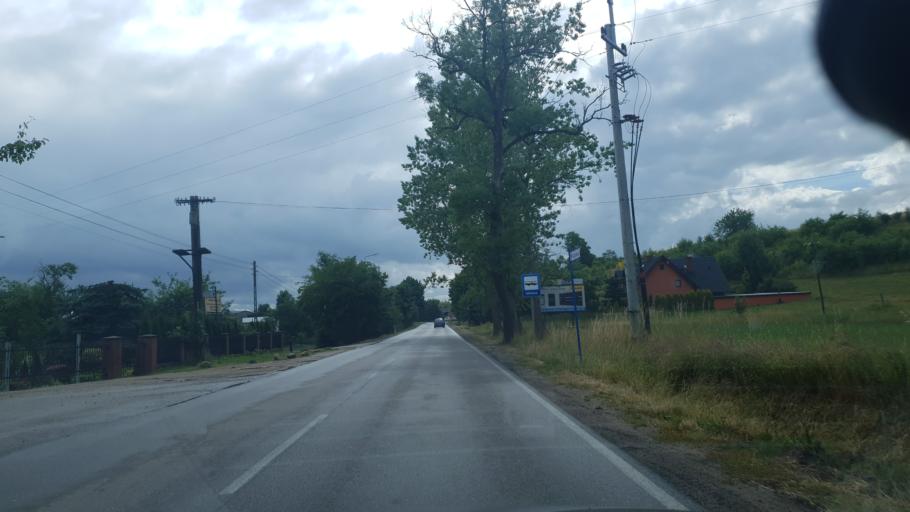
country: PL
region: Pomeranian Voivodeship
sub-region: Powiat kartuski
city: Chmielno
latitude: 54.2913
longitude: 18.1283
